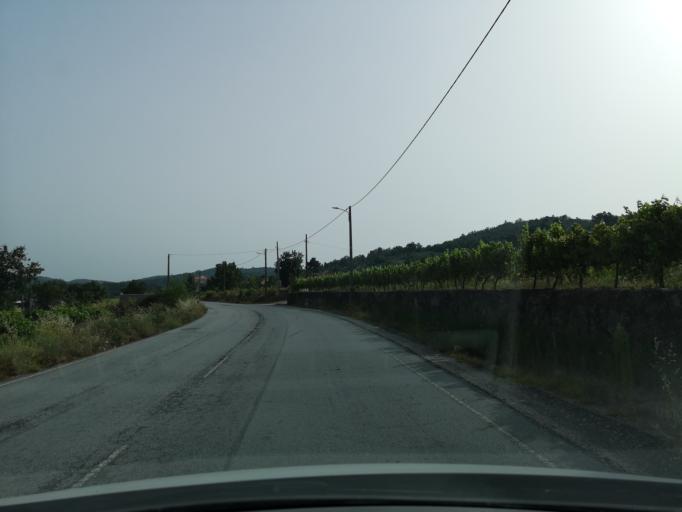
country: PT
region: Castelo Branco
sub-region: Belmonte
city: Belmonte
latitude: 40.3670
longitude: -7.3344
